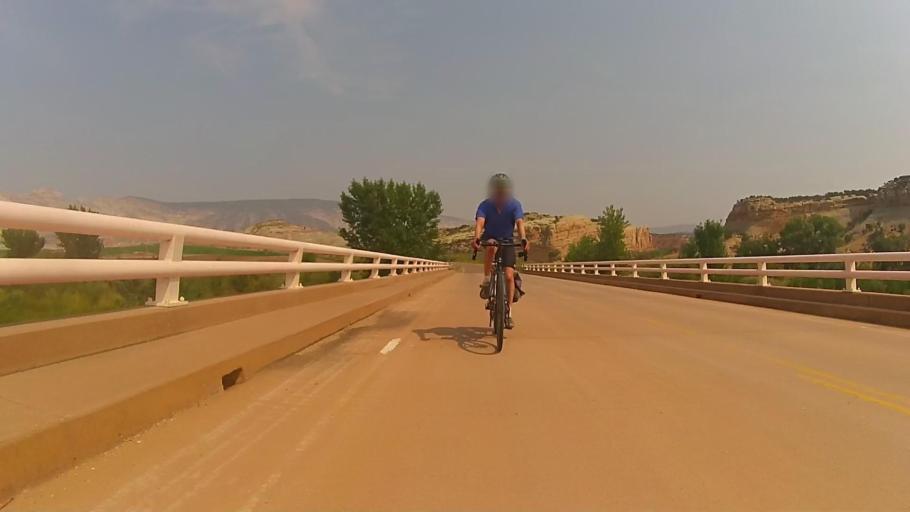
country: US
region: Utah
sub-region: Uintah County
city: Naples
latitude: 40.4088
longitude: -109.2344
